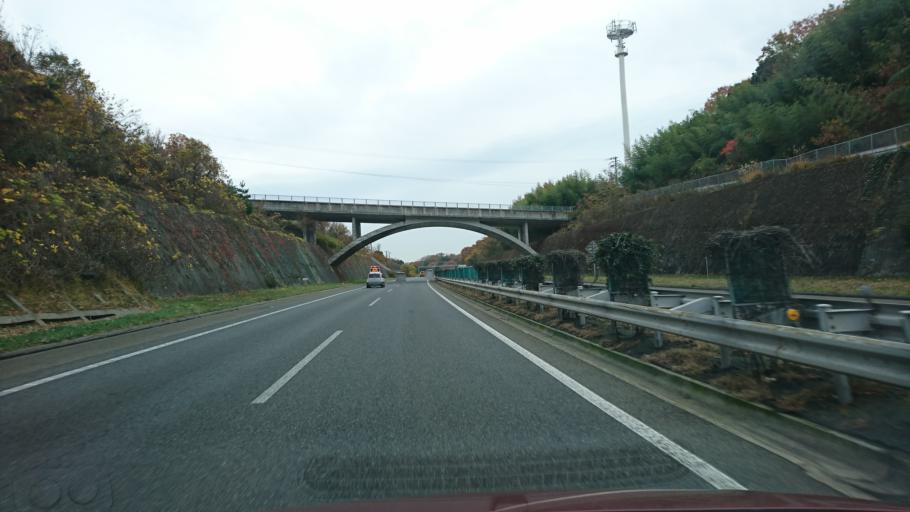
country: JP
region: Hyogo
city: Miki
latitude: 34.8214
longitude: 135.1083
